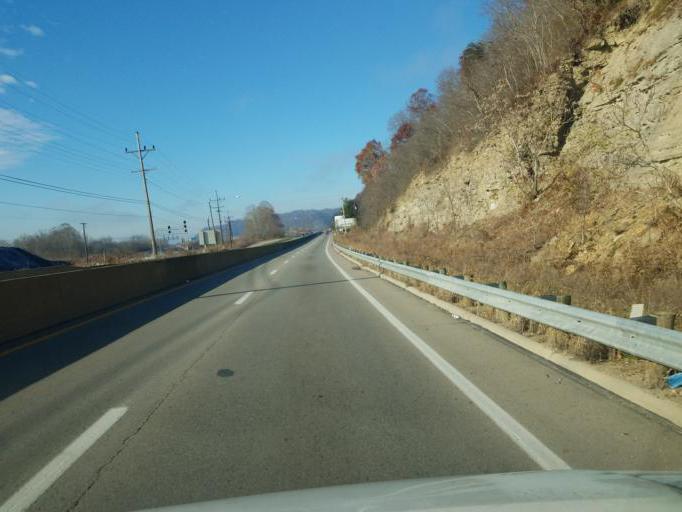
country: US
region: Ohio
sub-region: Scioto County
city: New Boston
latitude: 38.7557
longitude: -82.9072
